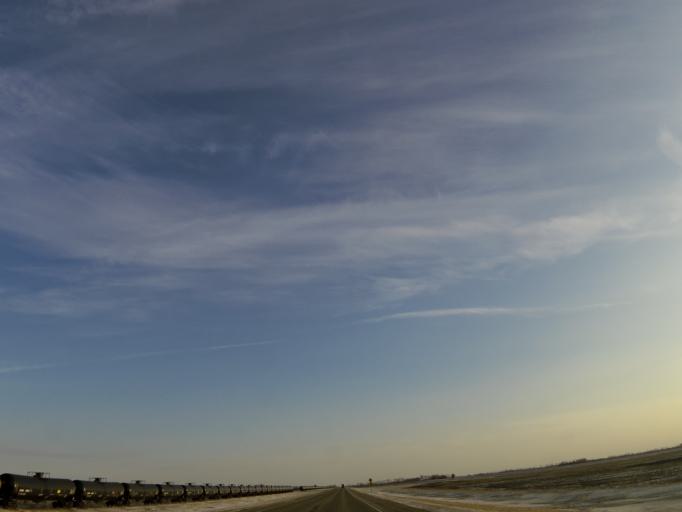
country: US
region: North Dakota
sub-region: Walsh County
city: Grafton
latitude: 48.5035
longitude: -97.4370
